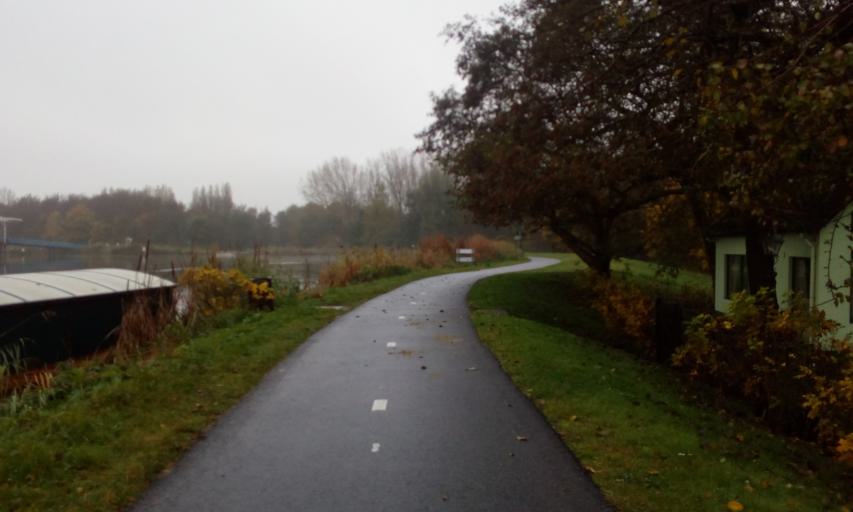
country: NL
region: South Holland
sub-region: Gemeente Lansingerland
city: Bleiswijk
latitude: 51.9924
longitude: 4.5473
